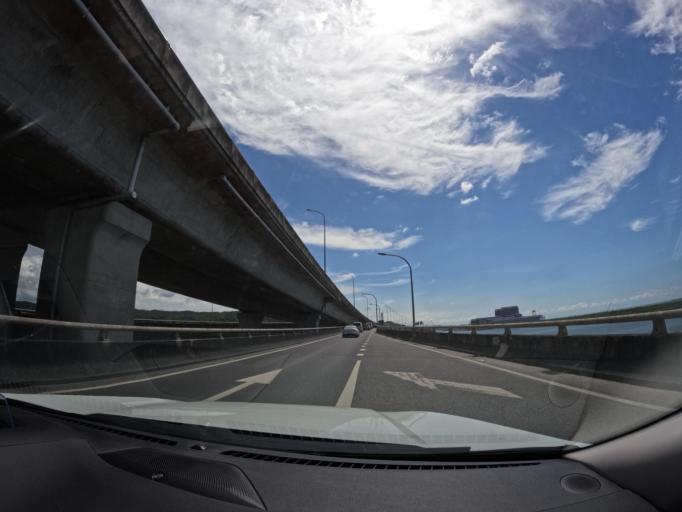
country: TW
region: Taipei
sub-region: Taipei
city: Banqiao
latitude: 25.1465
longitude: 121.3876
